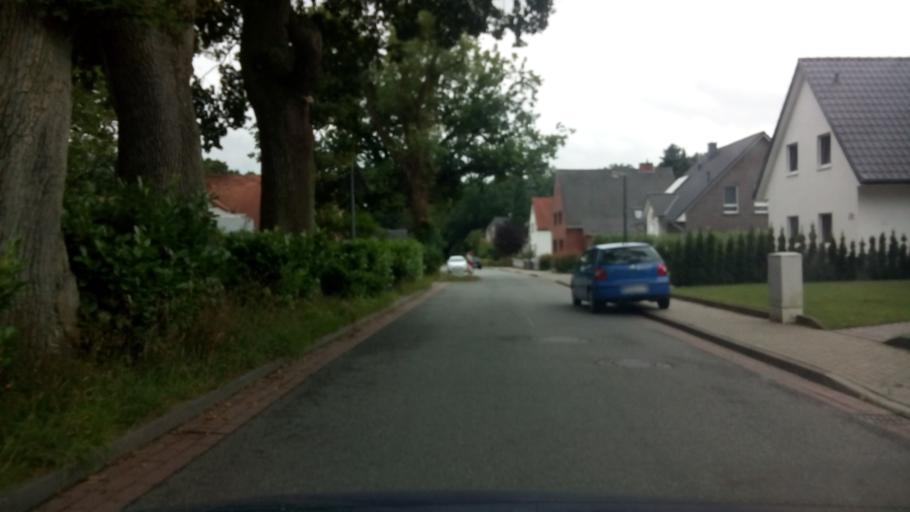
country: DE
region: Lower Saxony
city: Lemwerder
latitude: 53.1907
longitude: 8.6150
